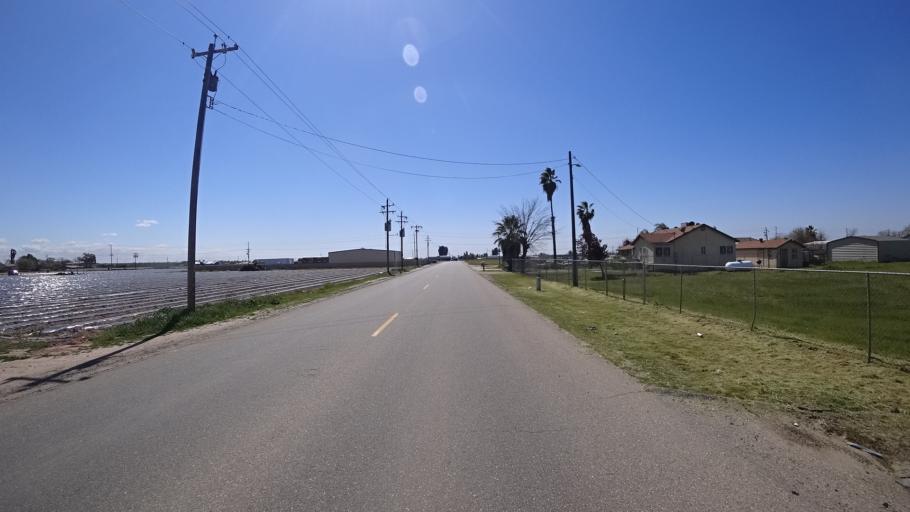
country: US
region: California
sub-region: Fresno County
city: West Park
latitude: 36.7084
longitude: -119.8445
